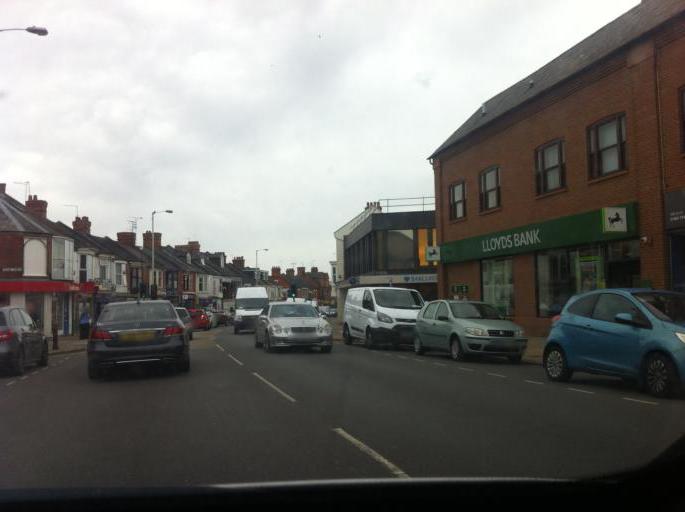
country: GB
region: England
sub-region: Northamptonshire
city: Northampton
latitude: 52.2426
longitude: -0.8743
